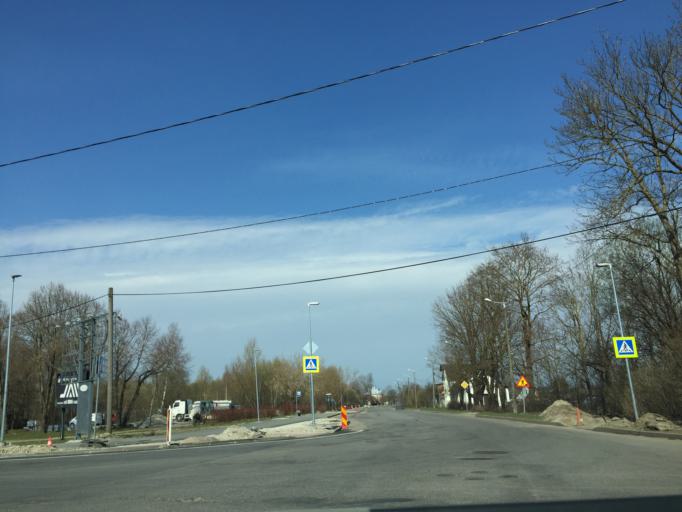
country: EE
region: Ida-Virumaa
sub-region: Narva linn
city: Narva
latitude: 59.3865
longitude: 28.1981
